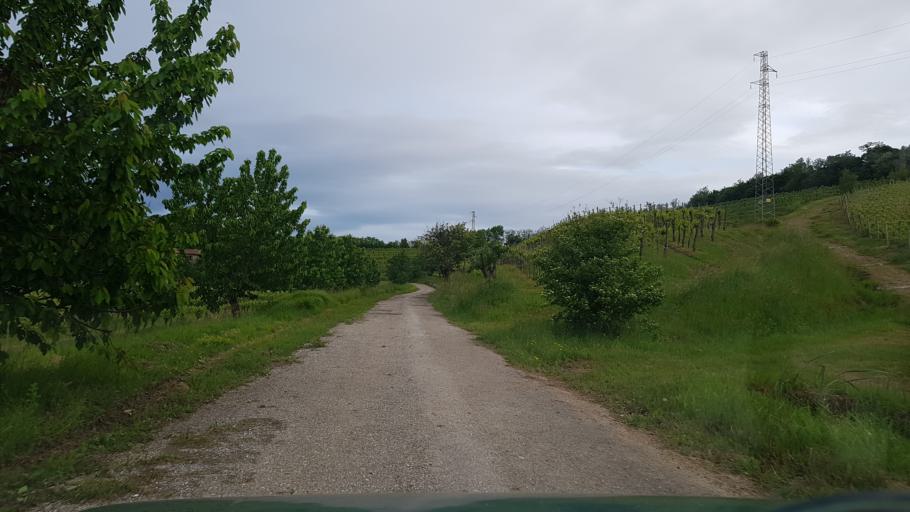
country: IT
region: Friuli Venezia Giulia
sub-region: Provincia di Gorizia
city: Farra d'Isonzo
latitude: 45.9096
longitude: 13.5290
